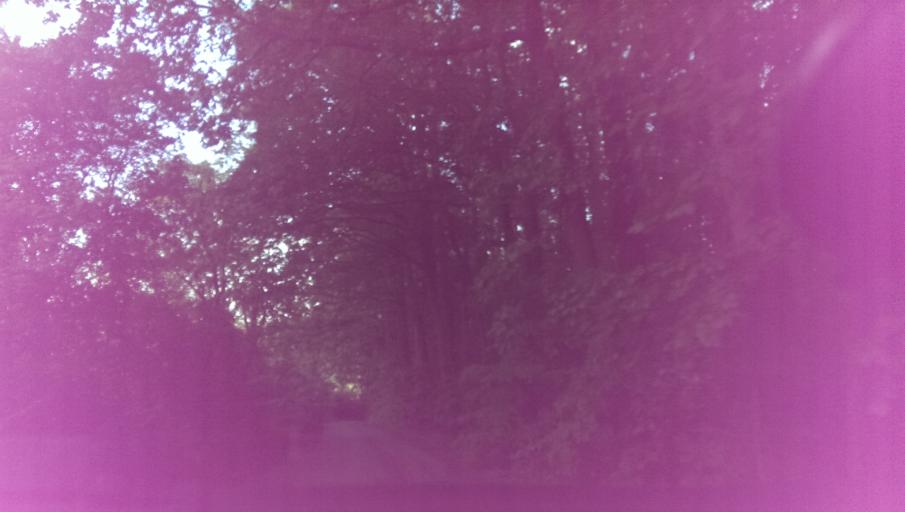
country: CZ
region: Zlin
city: Brezolupy
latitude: 49.1437
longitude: 17.5984
